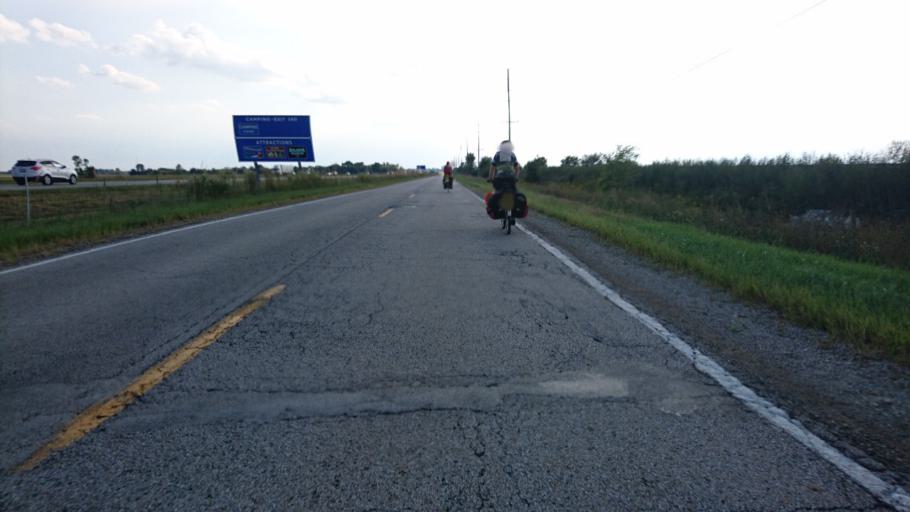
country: US
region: Illinois
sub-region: Logan County
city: Atlanta
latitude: 40.2896
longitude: -89.1984
